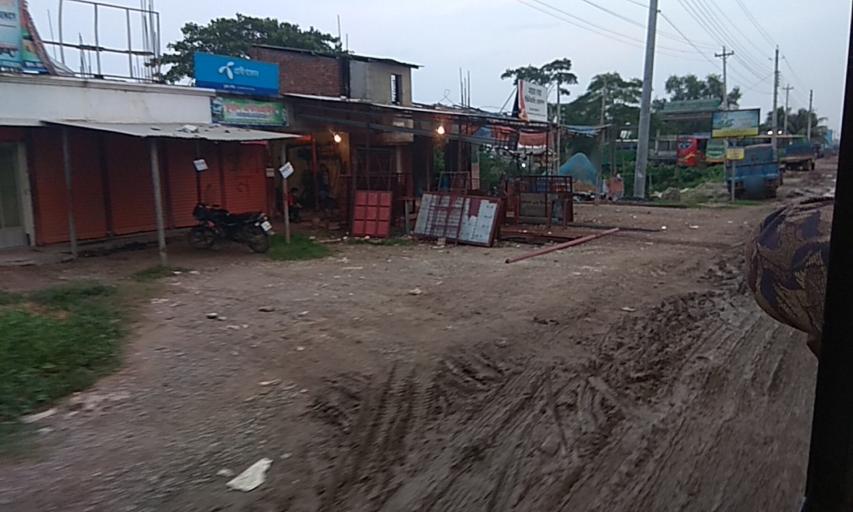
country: BD
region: Dhaka
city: Char Bhadrasan
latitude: 23.3861
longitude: 89.9936
